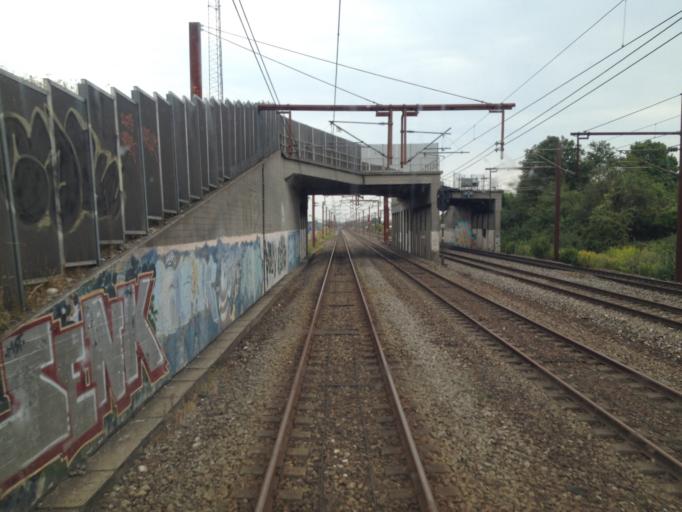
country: DK
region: Capital Region
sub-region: Albertslund Kommune
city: Albertslund
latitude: 55.6604
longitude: 12.3743
